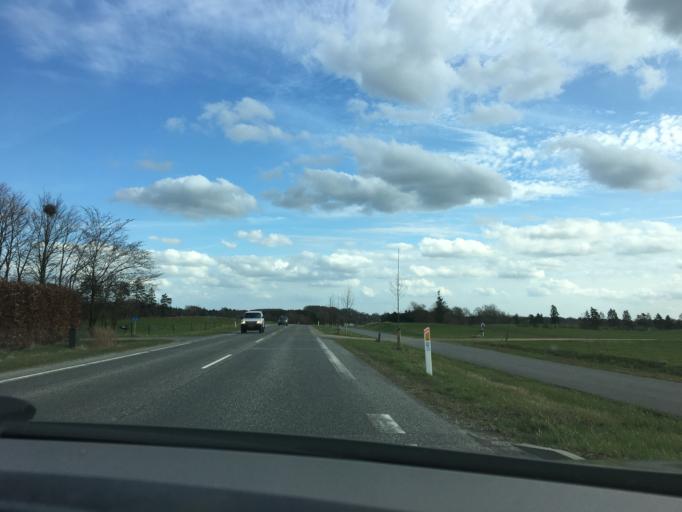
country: DK
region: South Denmark
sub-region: Vejle Kommune
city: Give
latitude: 55.8241
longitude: 9.3324
